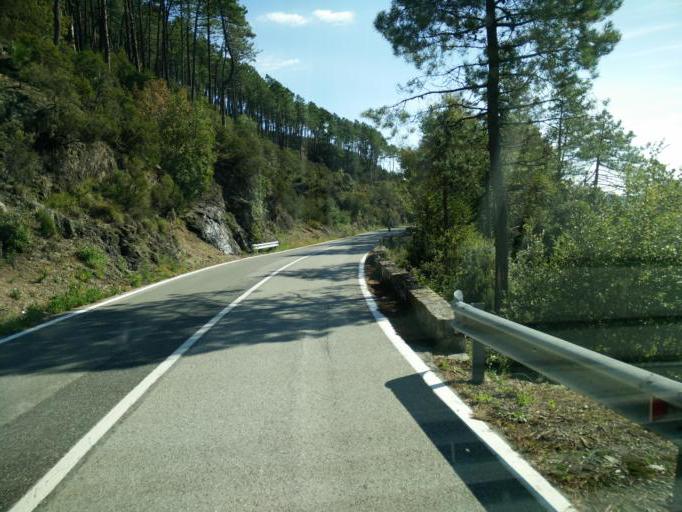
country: IT
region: Liguria
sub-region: Provincia di La Spezia
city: Carrodano
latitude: 44.2493
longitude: 9.6099
